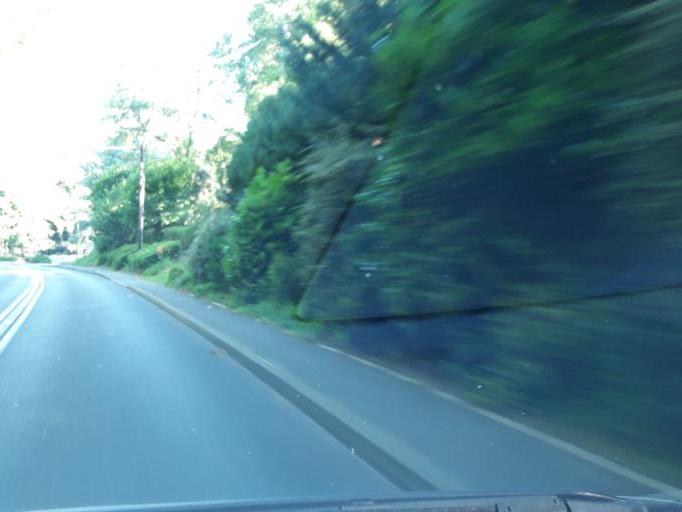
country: FR
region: Ile-de-France
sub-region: Departement de l'Essonne
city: Itteville
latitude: 48.5269
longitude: 2.3454
